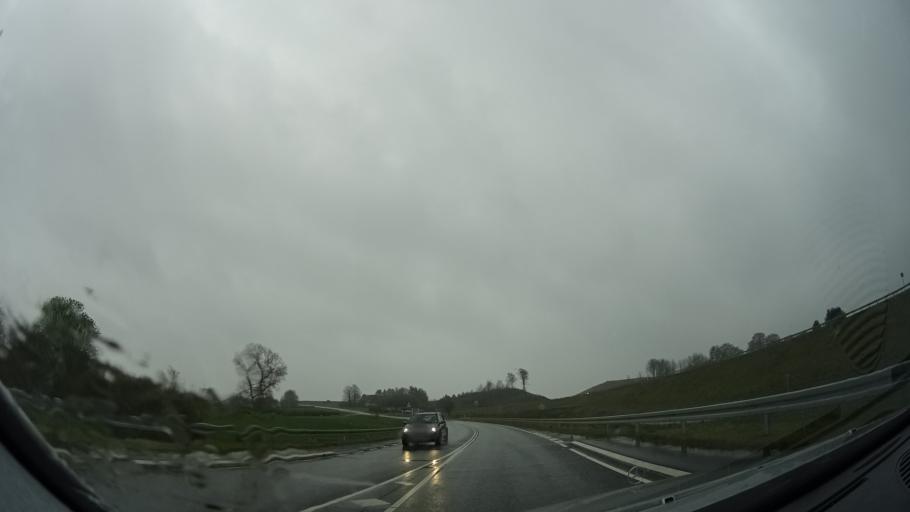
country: DK
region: Zealand
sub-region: Odsherred Kommune
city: Asnaes
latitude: 55.8152
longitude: 11.5848
